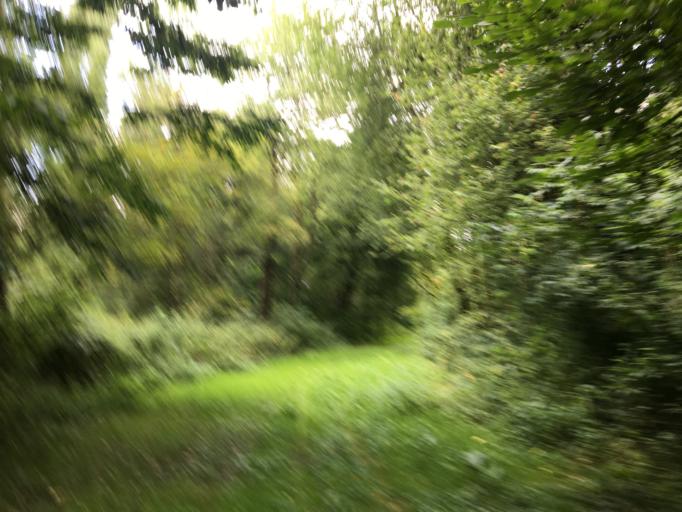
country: NL
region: Flevoland
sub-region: Gemeente Zeewolde
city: Zeewolde
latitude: 52.2803
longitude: 5.5198
